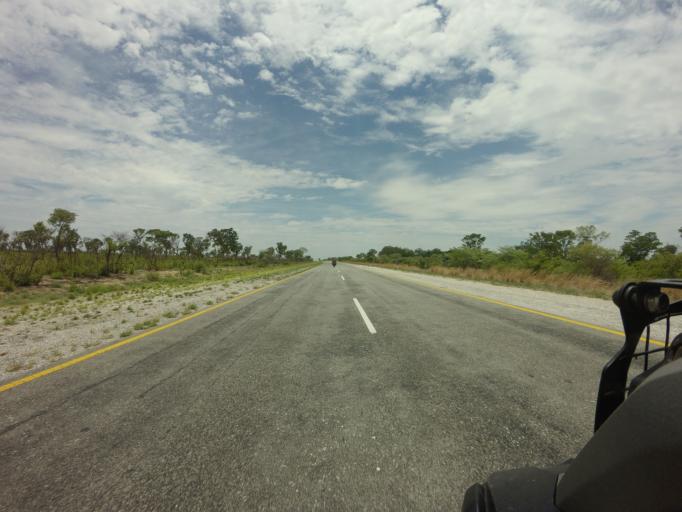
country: BW
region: North West
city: Shakawe
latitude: -18.0581
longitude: 22.1065
